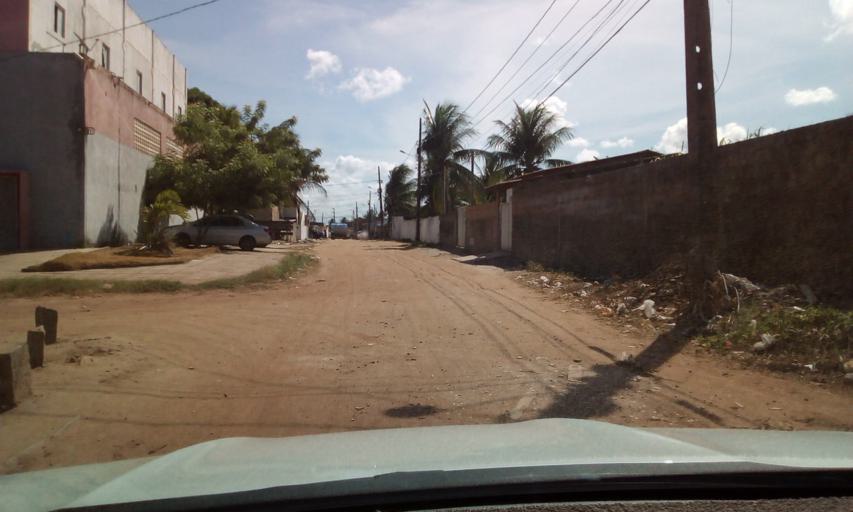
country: BR
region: Paraiba
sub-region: Joao Pessoa
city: Joao Pessoa
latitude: -7.1615
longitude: -34.8493
